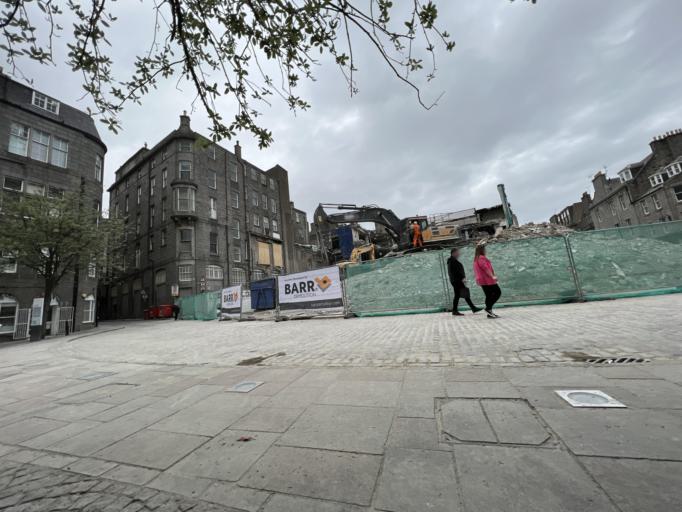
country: GB
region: Scotland
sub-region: Aberdeen City
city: Aberdeen
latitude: 57.1460
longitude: -2.0986
